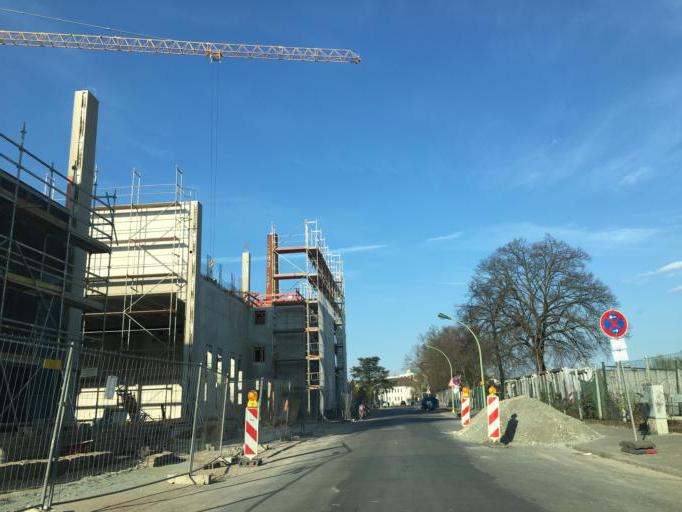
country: DE
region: Hesse
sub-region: Regierungsbezirk Darmstadt
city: Offenbach
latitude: 50.1182
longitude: 8.7377
